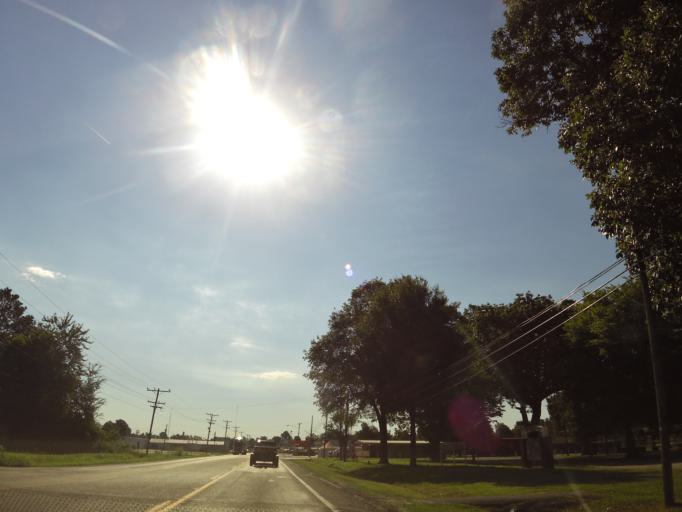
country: US
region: Arkansas
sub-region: Clay County
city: Corning
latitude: 36.4114
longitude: -90.5950
